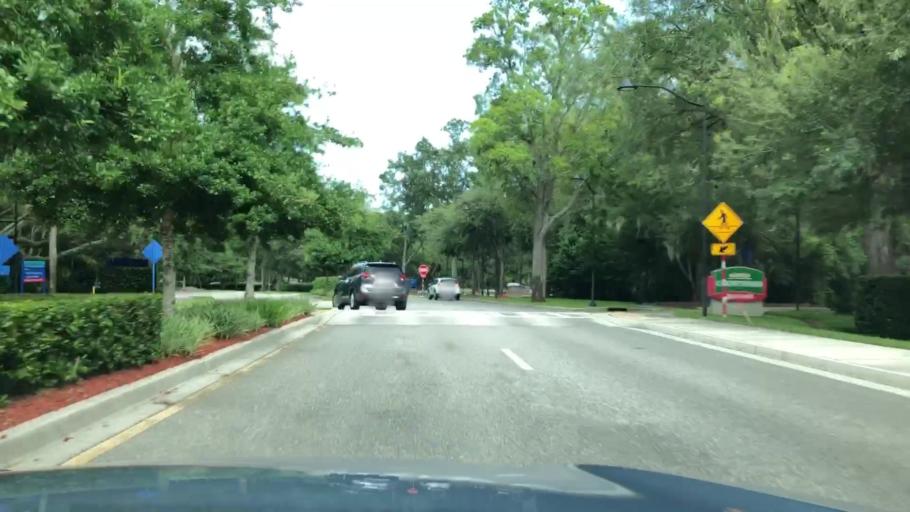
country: US
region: Florida
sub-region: Duval County
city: Jacksonville Beach
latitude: 30.2616
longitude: -81.4406
